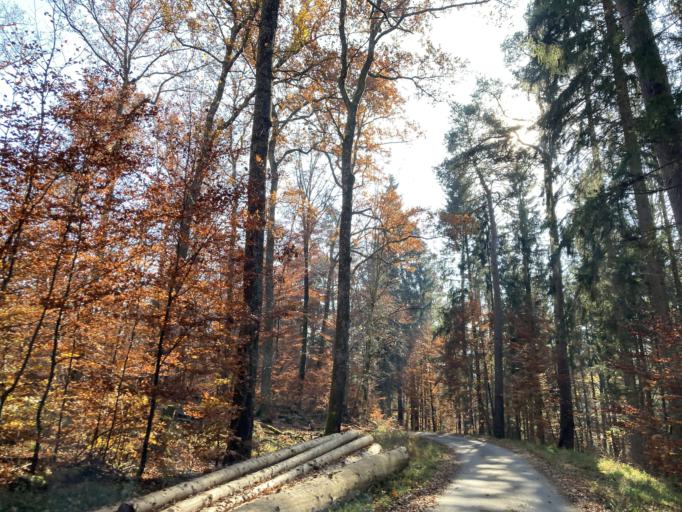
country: DE
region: Baden-Wuerttemberg
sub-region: Tuebingen Region
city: Tuebingen
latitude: 48.5675
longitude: 9.0628
